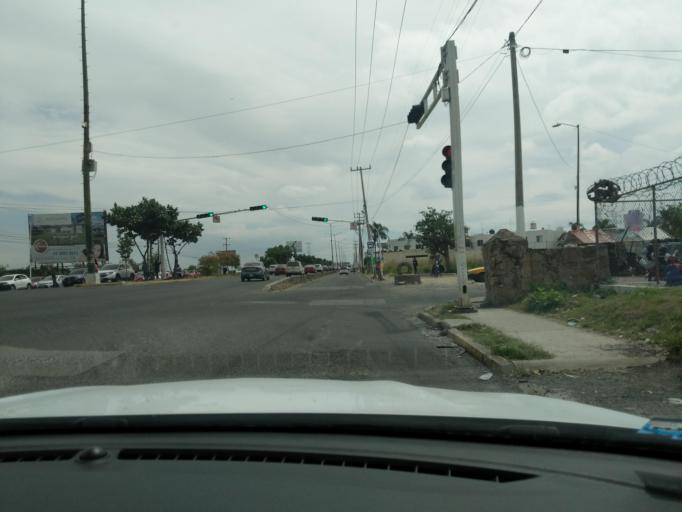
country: MX
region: Jalisco
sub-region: Zapopan
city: La Cuchilla (Extramuros de Tesistan)
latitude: 20.7817
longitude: -103.4633
